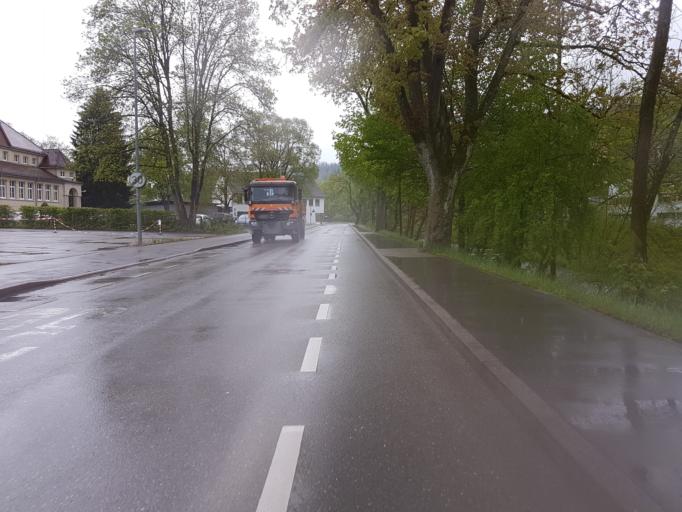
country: DE
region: Baden-Wuerttemberg
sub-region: Freiburg Region
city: Oberndorf
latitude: 48.2919
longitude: 8.5780
